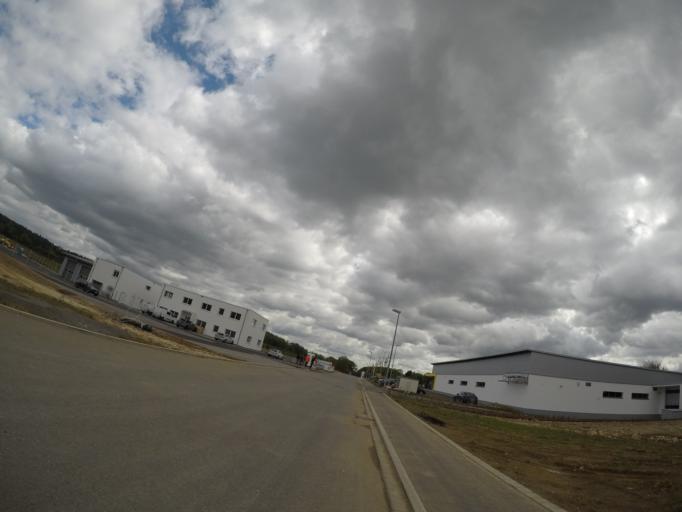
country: DE
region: Baden-Wuerttemberg
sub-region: Tuebingen Region
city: Beimerstetten
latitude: 48.4892
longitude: 9.9825
